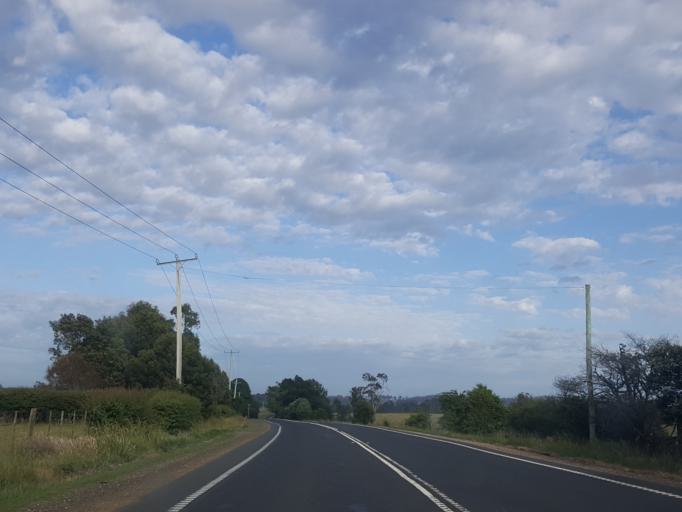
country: AU
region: Tasmania
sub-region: Northern Midlands
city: Perth
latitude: -41.5938
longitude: 147.2052
